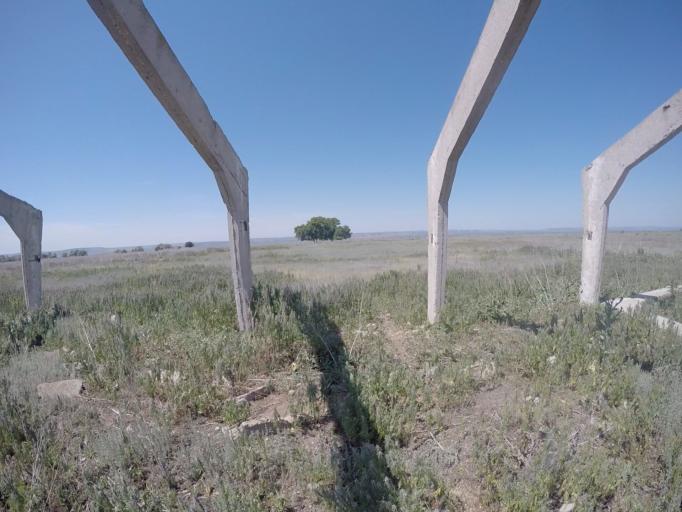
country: RU
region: Saratov
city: Krasnoarmeysk
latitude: 51.1689
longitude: 45.9081
